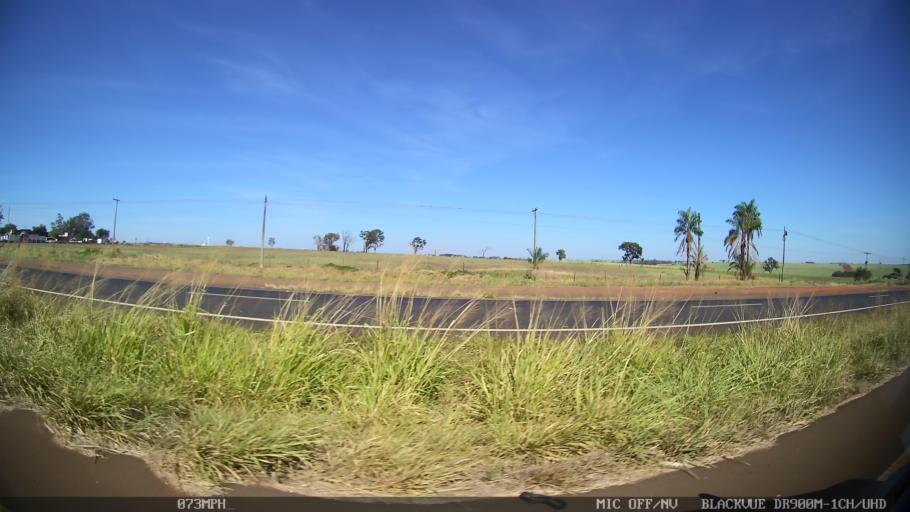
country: BR
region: Sao Paulo
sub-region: Barretos
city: Barretos
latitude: -20.5442
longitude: -48.6218
